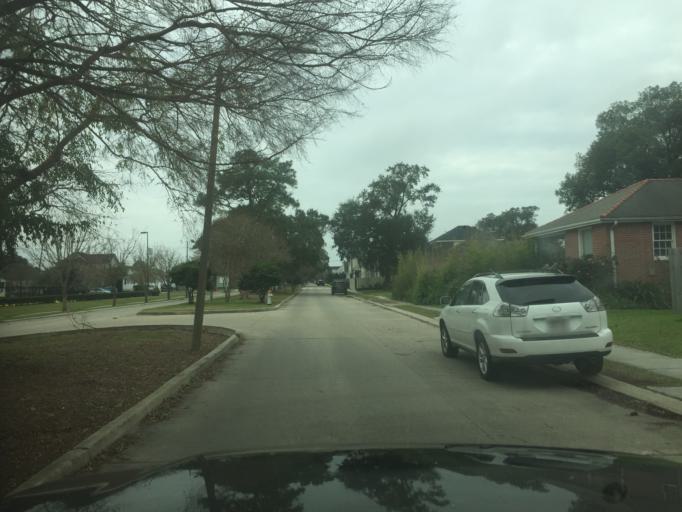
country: US
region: Louisiana
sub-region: Jefferson Parish
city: Metairie
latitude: 30.0035
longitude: -90.1029
